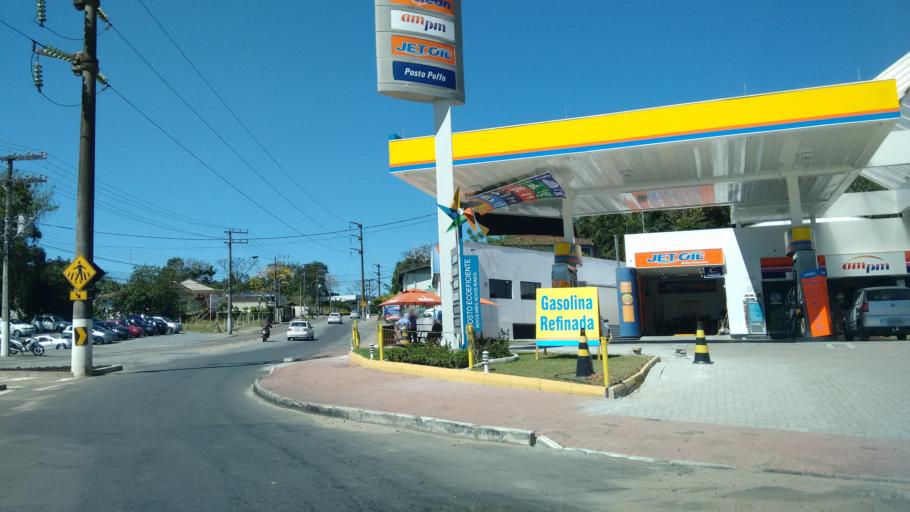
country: BR
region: Santa Catarina
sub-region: Blumenau
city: Blumenau
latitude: -26.8838
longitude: -49.1019
